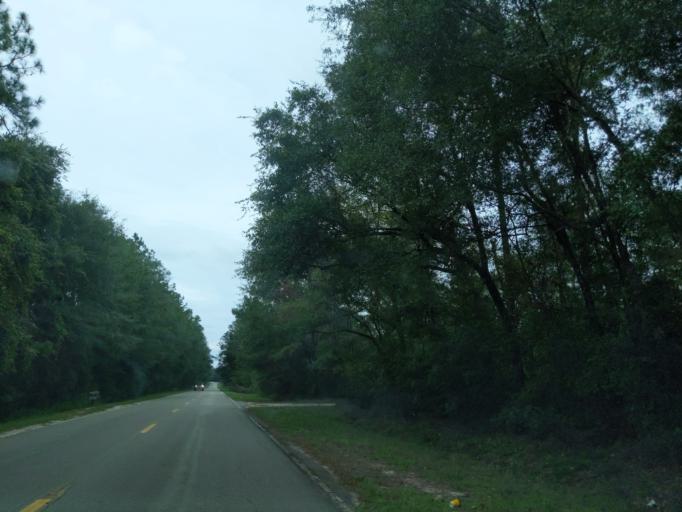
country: US
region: Florida
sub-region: Leon County
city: Woodville
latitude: 30.3736
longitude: -84.1470
